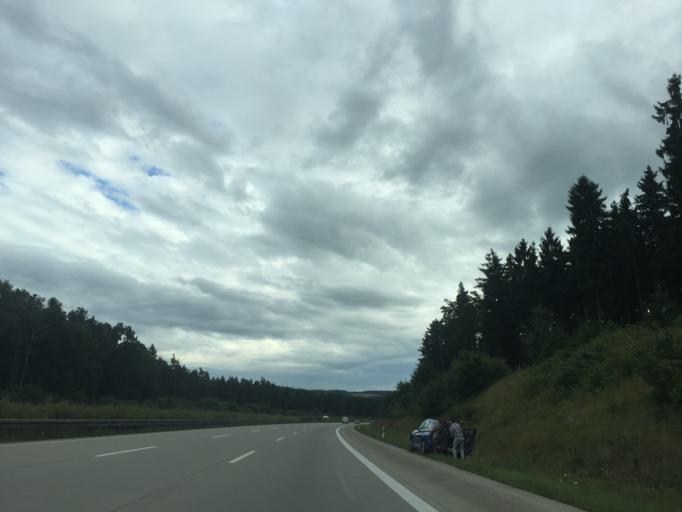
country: DE
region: Thuringia
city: Schleiz
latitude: 50.5337
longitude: 11.8049
